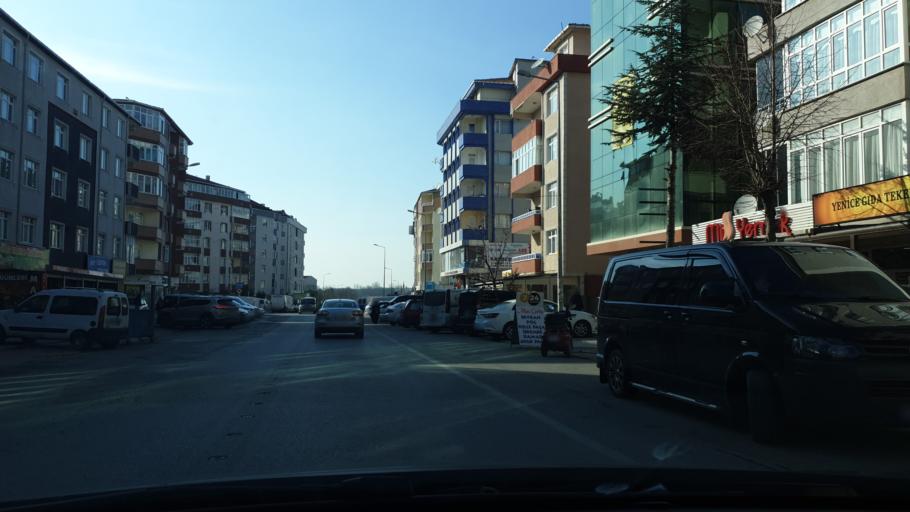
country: TR
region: Tekirdag
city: Cerkezkoey
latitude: 41.2881
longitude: 27.9888
